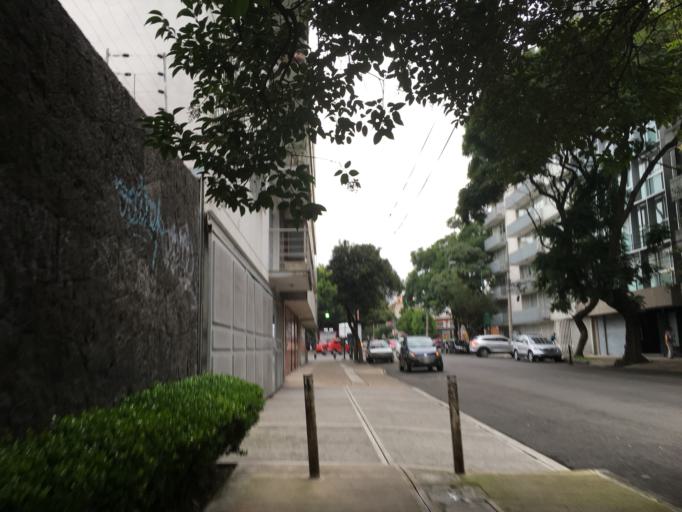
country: MX
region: Mexico City
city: Colonia del Valle
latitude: 19.3788
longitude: -99.1703
